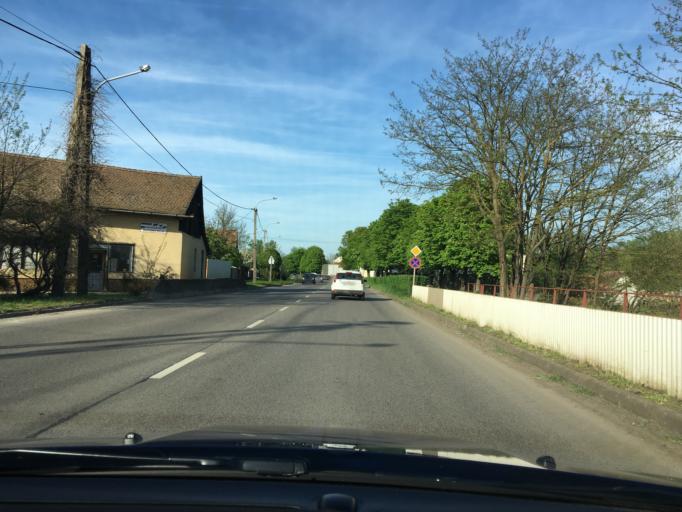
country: HU
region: Bekes
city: Korosladany
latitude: 46.9631
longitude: 21.0857
